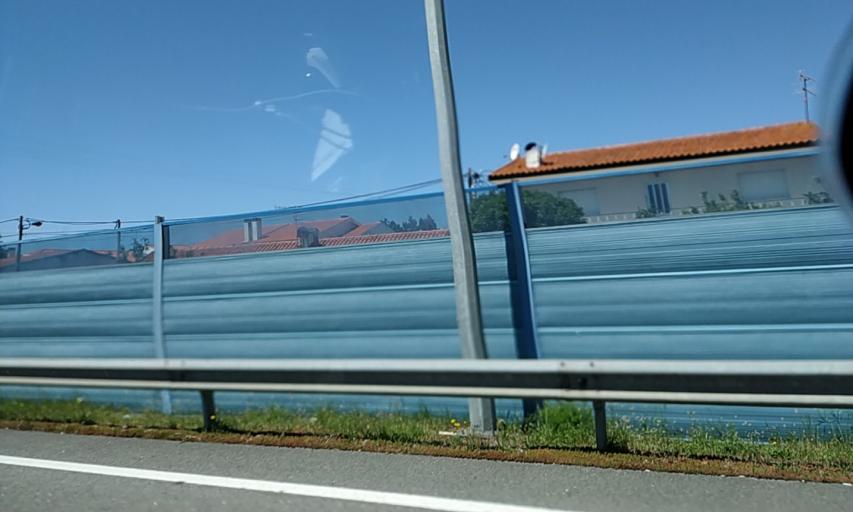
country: PT
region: Aveiro
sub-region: Ilhavo
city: Gafanha da Nazare
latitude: 40.6287
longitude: -8.7033
